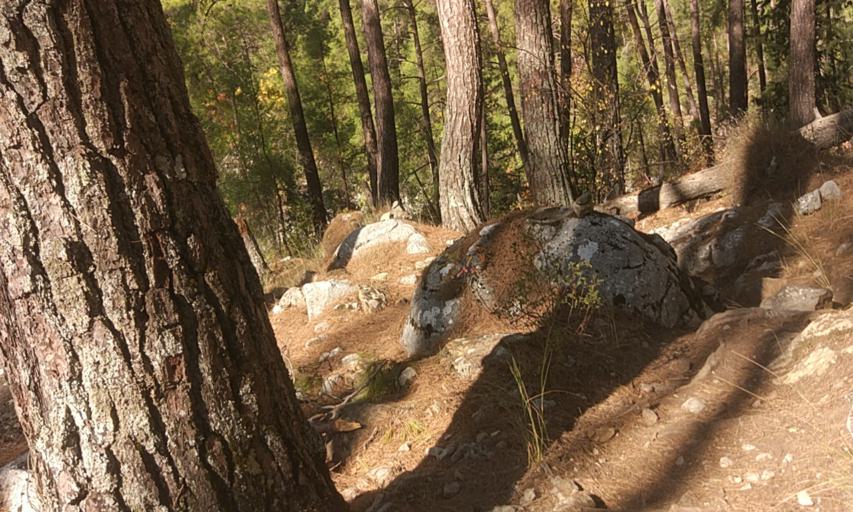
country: TR
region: Antalya
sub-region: Kemer
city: Goeynuek
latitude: 36.6757
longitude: 30.4955
